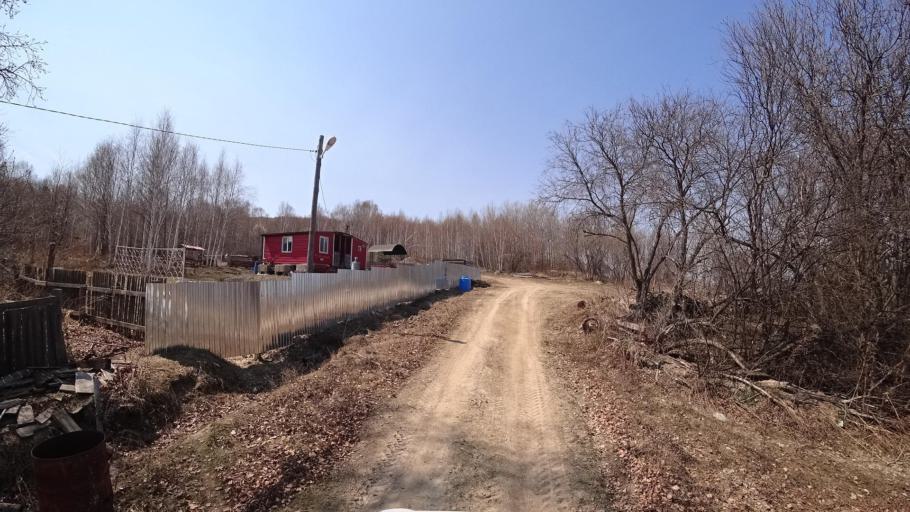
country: RU
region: Khabarovsk Krai
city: Selikhino
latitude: 50.6711
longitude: 137.3943
